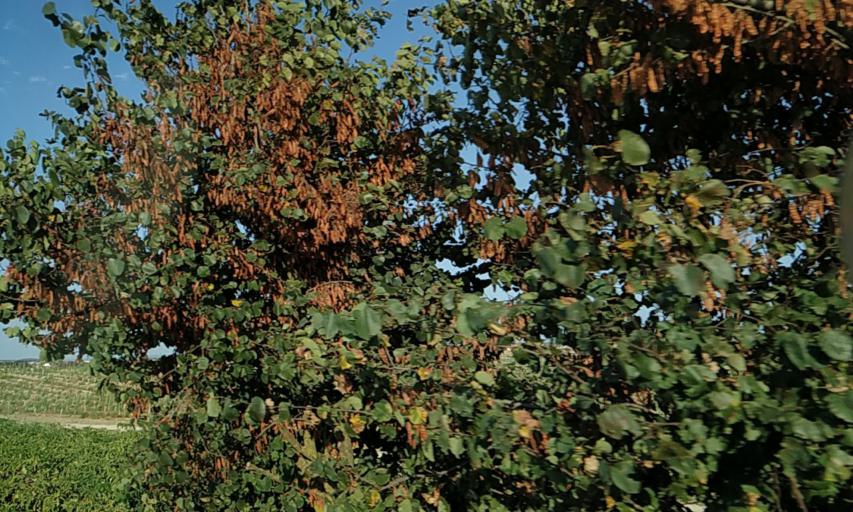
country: PT
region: Santarem
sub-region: Santarem
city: Santarem
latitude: 39.3411
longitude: -8.6615
